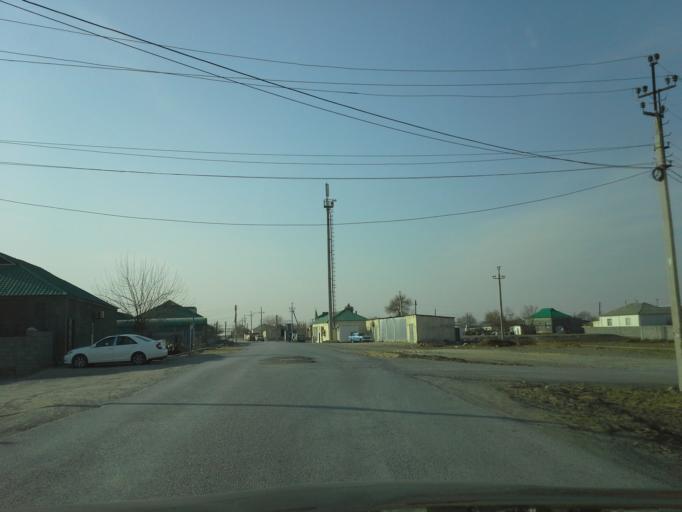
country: TM
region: Ahal
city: Abadan
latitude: 38.1732
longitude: 58.0448
